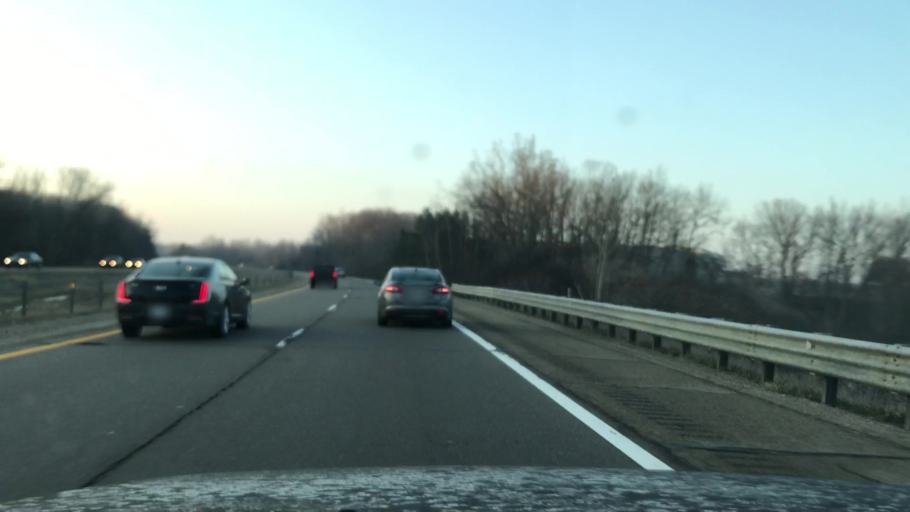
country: US
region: Michigan
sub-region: Kent County
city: East Grand Rapids
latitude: 42.9360
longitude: -85.5660
